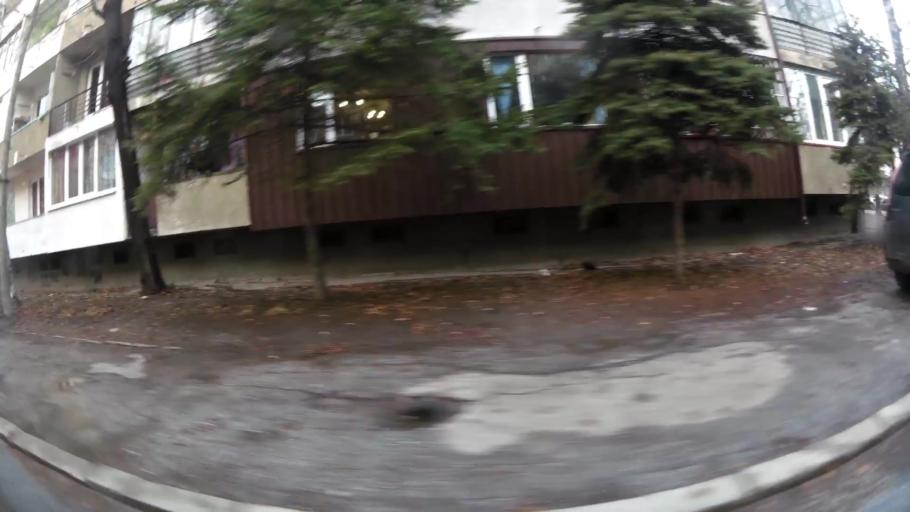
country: BG
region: Sofia-Capital
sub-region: Stolichna Obshtina
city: Sofia
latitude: 42.7289
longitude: 23.3112
